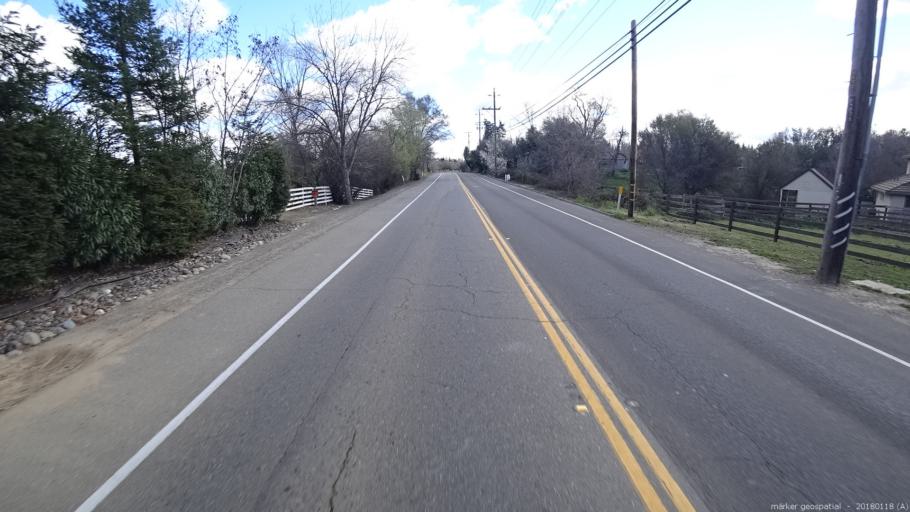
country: US
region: California
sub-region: Sacramento County
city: Folsom
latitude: 38.6997
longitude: -121.1962
